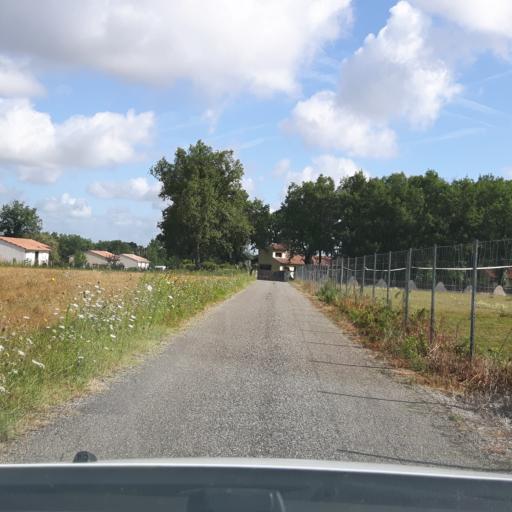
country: FR
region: Midi-Pyrenees
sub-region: Departement de la Haute-Garonne
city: Bouloc
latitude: 43.7982
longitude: 1.4103
